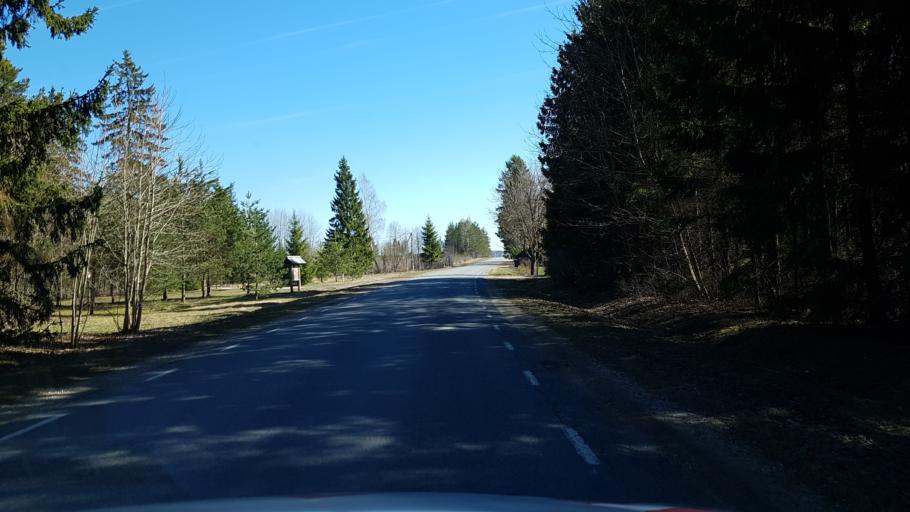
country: EE
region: Laeaene-Virumaa
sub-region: Someru vald
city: Someru
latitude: 59.3615
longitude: 26.4686
